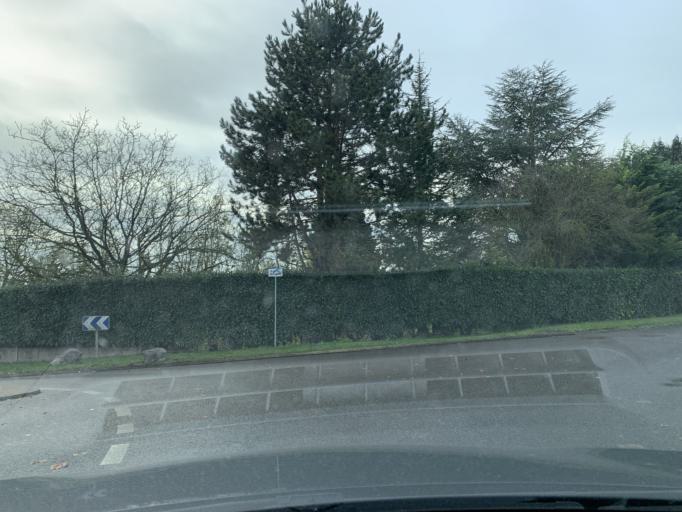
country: FR
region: Nord-Pas-de-Calais
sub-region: Departement du Nord
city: Neuville-Saint-Remy
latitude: 50.1846
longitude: 3.2155
